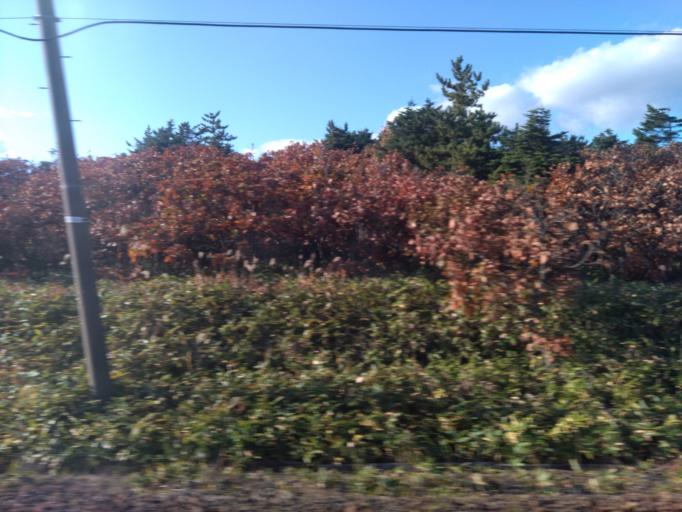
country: JP
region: Hokkaido
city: Niseko Town
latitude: 42.5650
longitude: 140.4351
